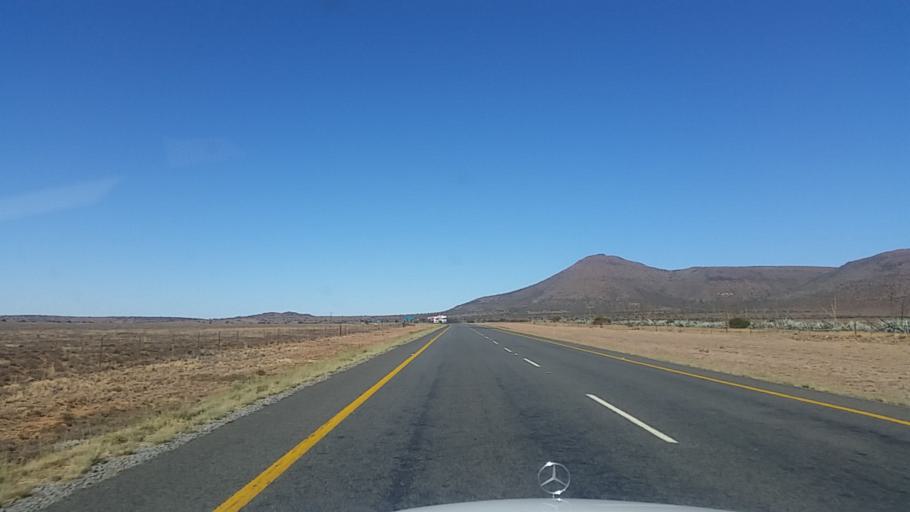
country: ZA
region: Eastern Cape
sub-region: Cacadu District Municipality
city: Graaff-Reinet
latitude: -32.0270
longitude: 24.6306
